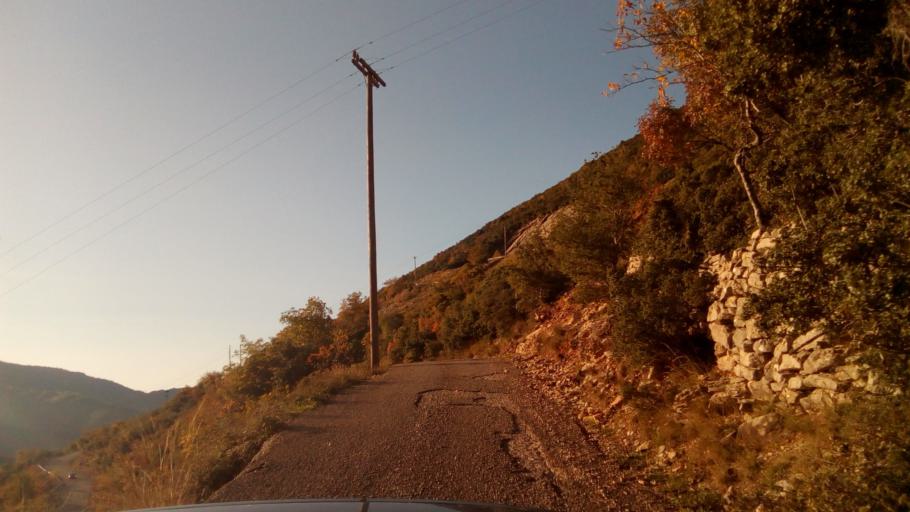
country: GR
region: West Greece
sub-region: Nomos Aitolias kai Akarnanias
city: Thermo
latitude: 38.5897
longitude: 21.7967
